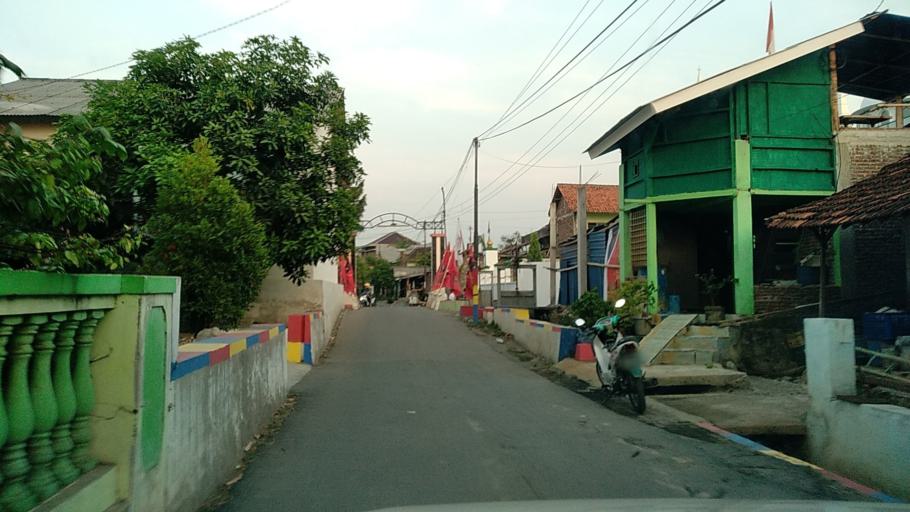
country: ID
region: Central Java
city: Semarang
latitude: -6.9706
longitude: 110.3059
